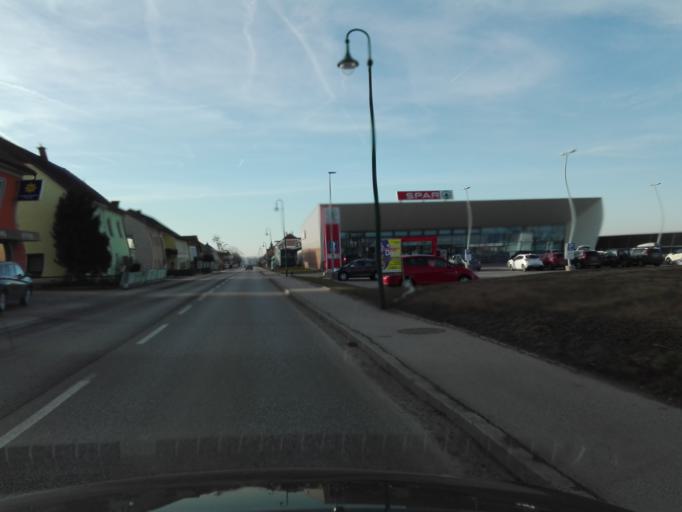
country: AT
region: Lower Austria
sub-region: Politischer Bezirk Amstetten
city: Strengberg
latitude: 48.1445
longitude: 14.6443
